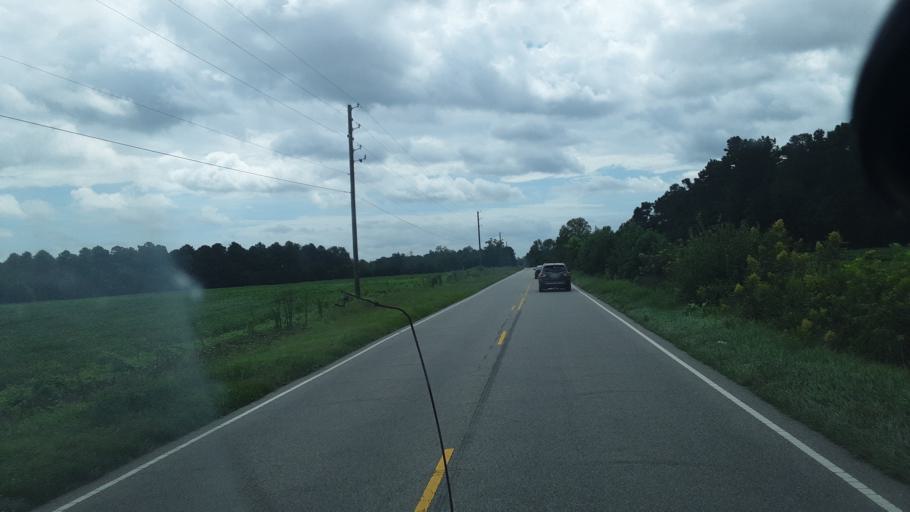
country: US
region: North Carolina
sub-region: Scotland County
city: Laurinburg
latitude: 34.7096
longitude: -79.4482
